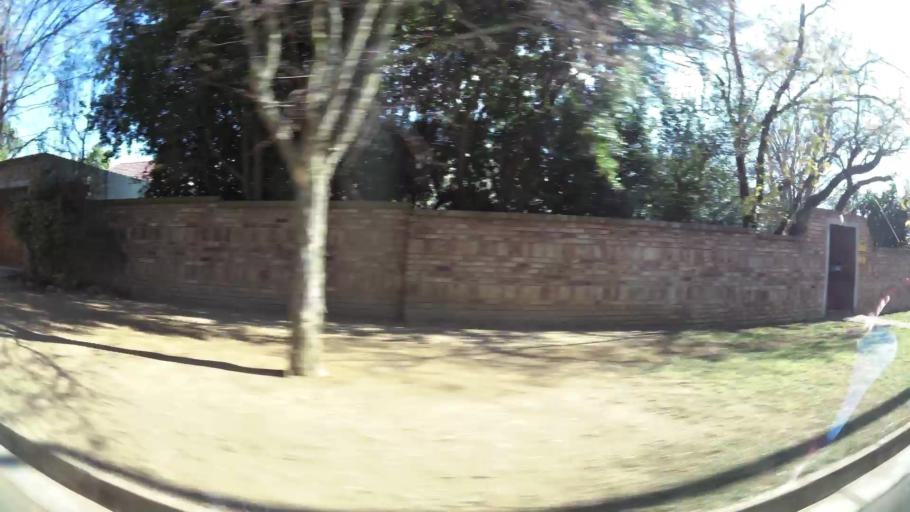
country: ZA
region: Gauteng
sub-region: Ekurhuleni Metropolitan Municipality
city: Benoni
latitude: -26.1435
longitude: 28.3429
